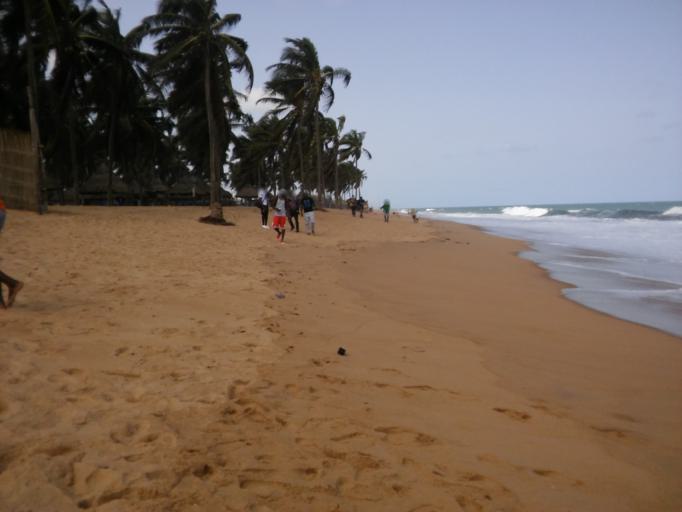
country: TG
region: Maritime
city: Lome
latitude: 6.1660
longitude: 1.3459
